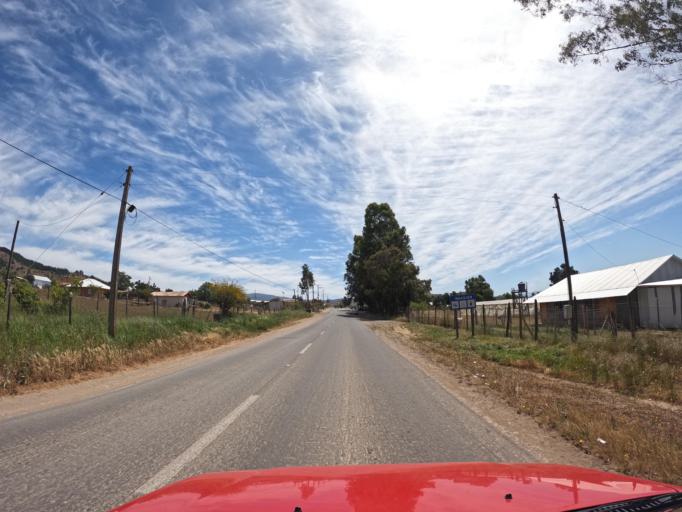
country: CL
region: Maule
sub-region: Provincia de Talca
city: Talca
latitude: -35.1216
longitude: -71.6761
